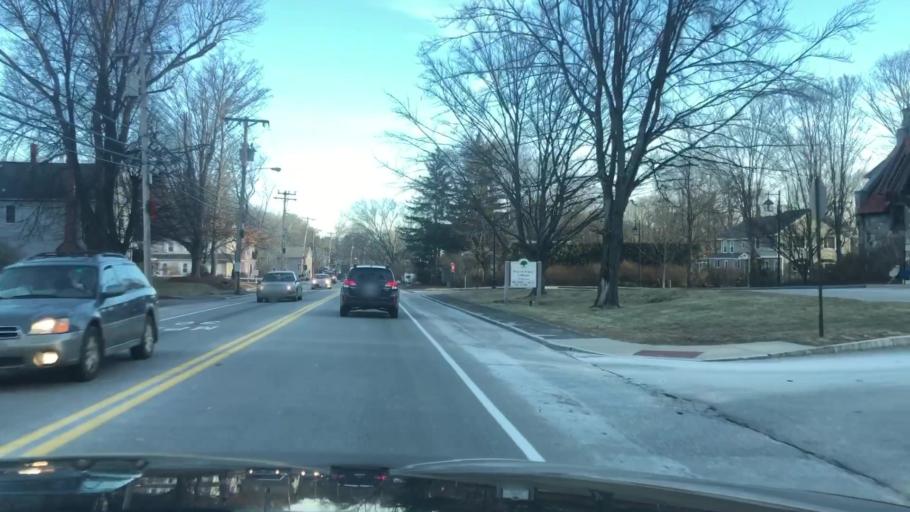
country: US
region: Massachusetts
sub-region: Worcester County
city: Bolton
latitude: 42.4350
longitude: -71.6116
